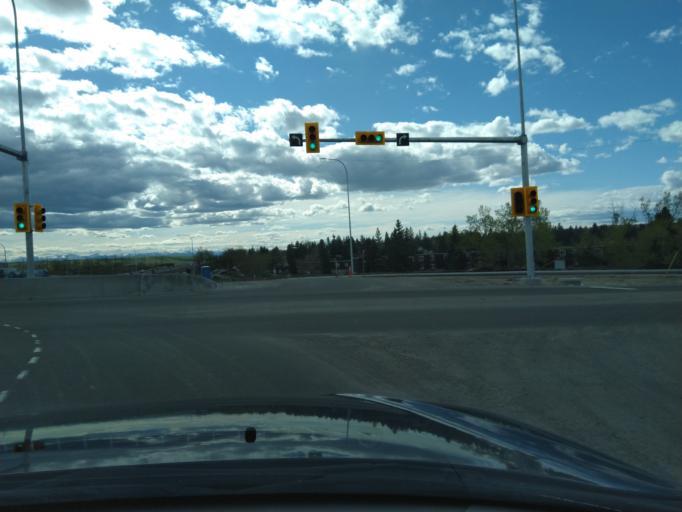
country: CA
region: Alberta
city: Calgary
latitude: 51.0093
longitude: -114.1412
